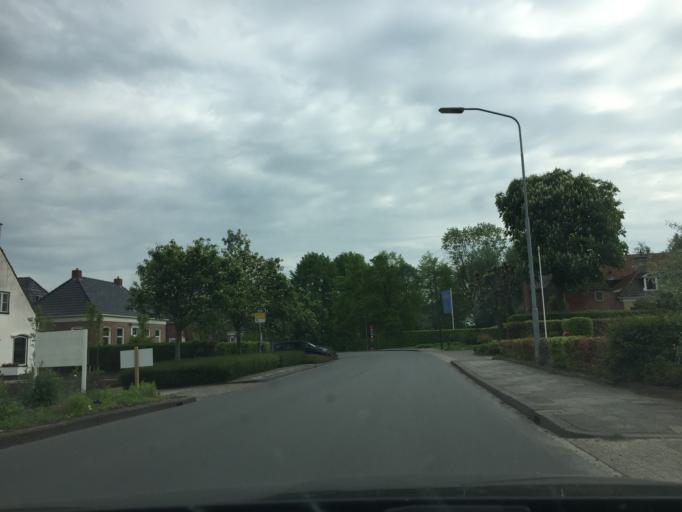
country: NL
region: Groningen
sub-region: Gemeente Zuidhorn
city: Aduard
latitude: 53.2589
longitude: 6.4581
